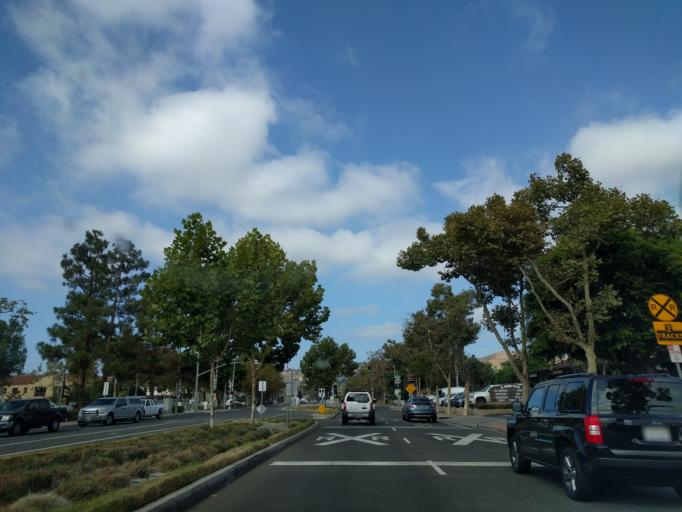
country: US
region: California
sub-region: Orange County
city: San Juan Capistrano
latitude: 33.4982
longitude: -117.6630
